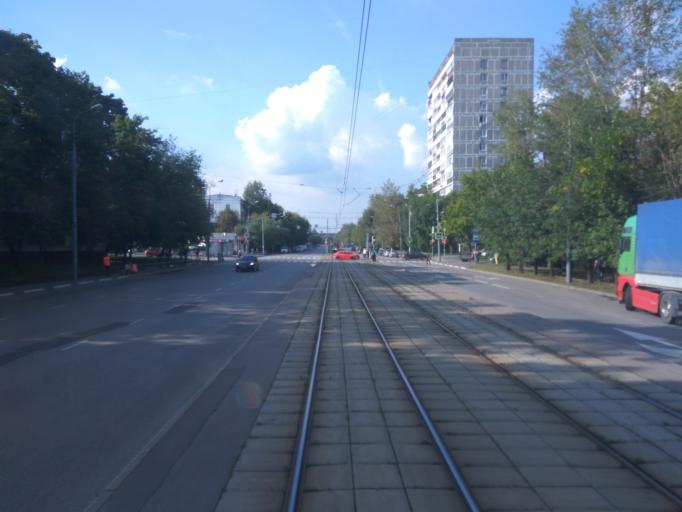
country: RU
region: Moscow
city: Perovo
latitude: 55.7555
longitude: 37.7897
